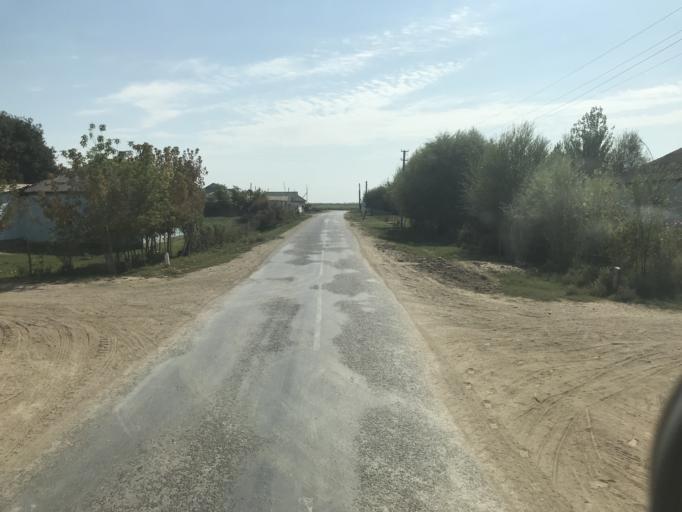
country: KZ
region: Ongtustik Qazaqstan
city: Myrzakent
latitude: 40.6641
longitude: 68.6303
